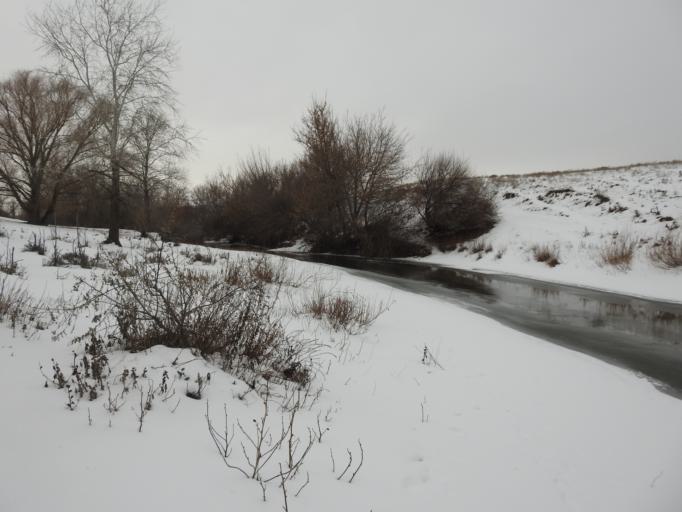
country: RU
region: Saratov
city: Krasnyy Yar
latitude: 51.5312
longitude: 46.5741
